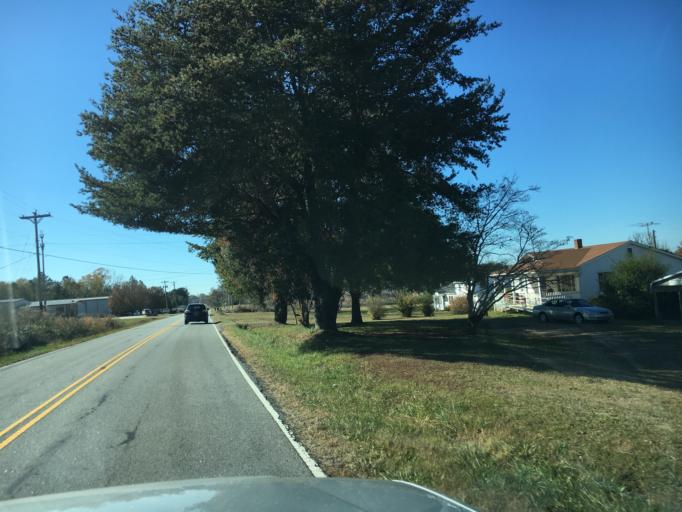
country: US
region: South Carolina
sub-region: Anderson County
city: Centerville
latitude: 34.5135
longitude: -82.7482
